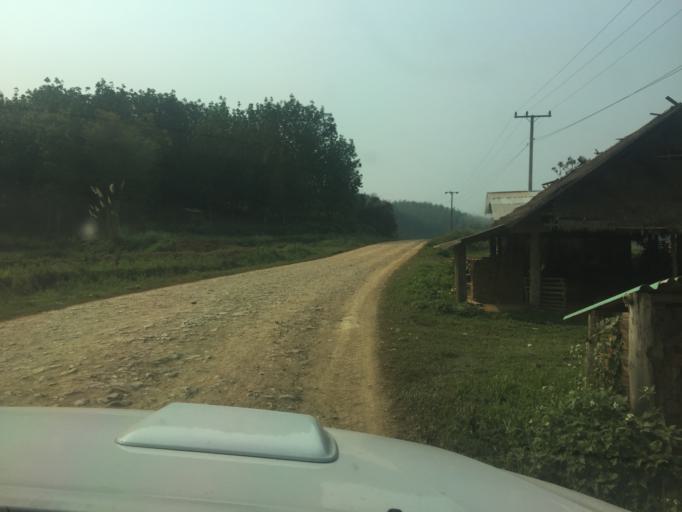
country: TH
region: Phayao
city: Phu Sang
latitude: 19.6682
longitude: 100.5282
